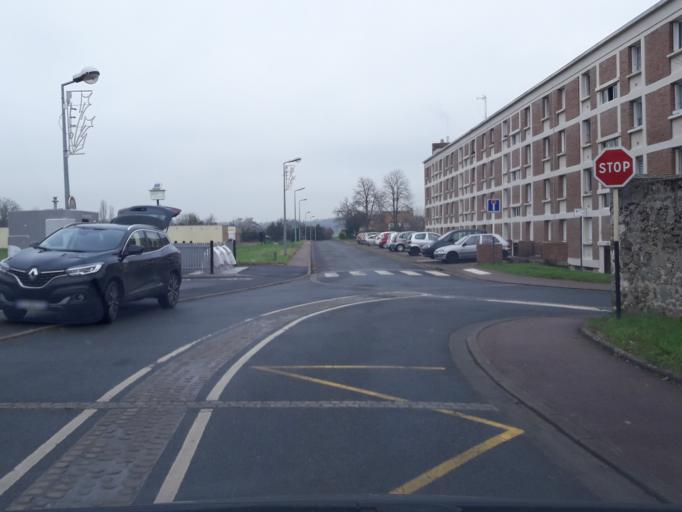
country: FR
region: Ile-de-France
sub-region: Departement de l'Essonne
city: Vert-le-Petit
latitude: 48.5567
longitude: 2.3703
